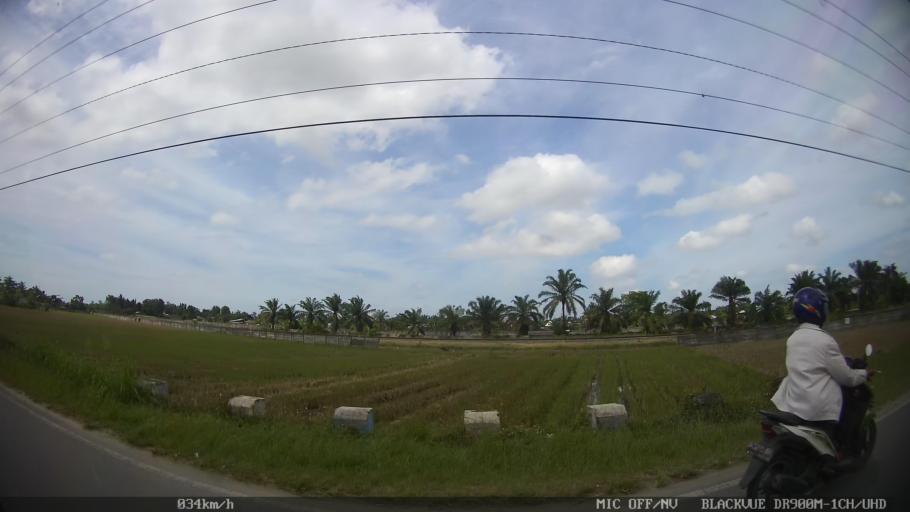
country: ID
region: North Sumatra
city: Percut
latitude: 3.6097
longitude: 98.8487
